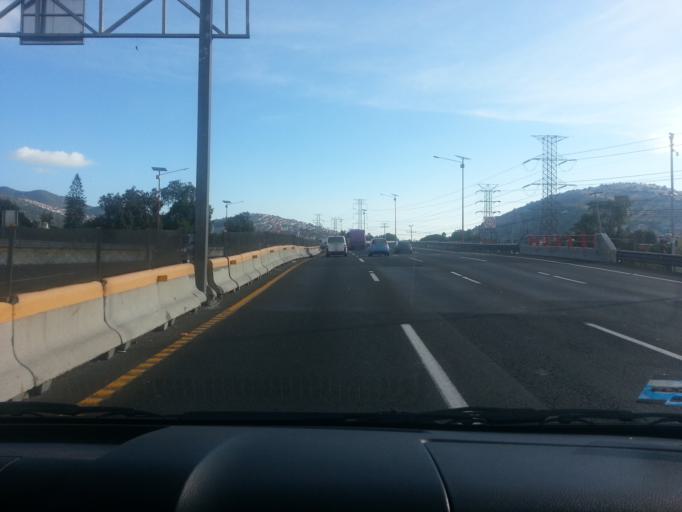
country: MX
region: Mexico
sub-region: Tlalnepantla de Baz
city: Puerto Escondido (Tepeolulco Puerto Escondido)
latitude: 19.5384
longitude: -99.0745
